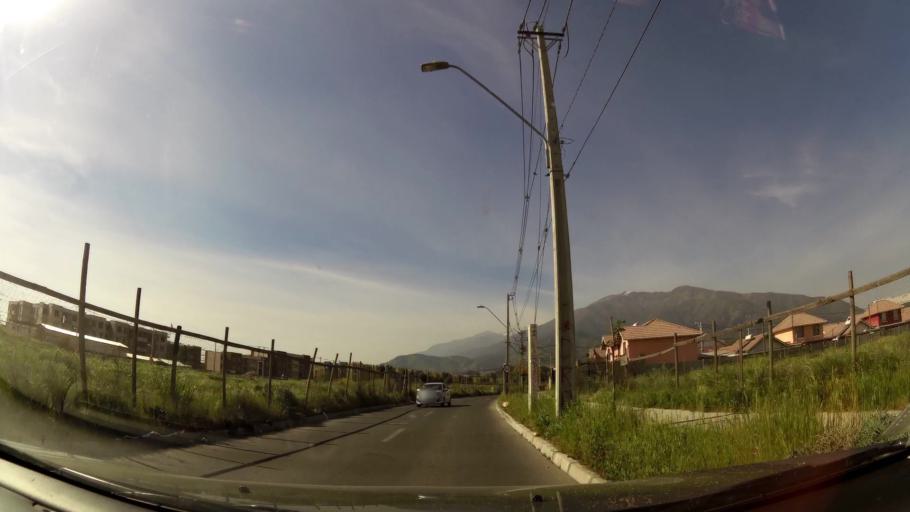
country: CL
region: Santiago Metropolitan
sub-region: Provincia de Cordillera
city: Puente Alto
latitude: -33.5907
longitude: -70.5513
